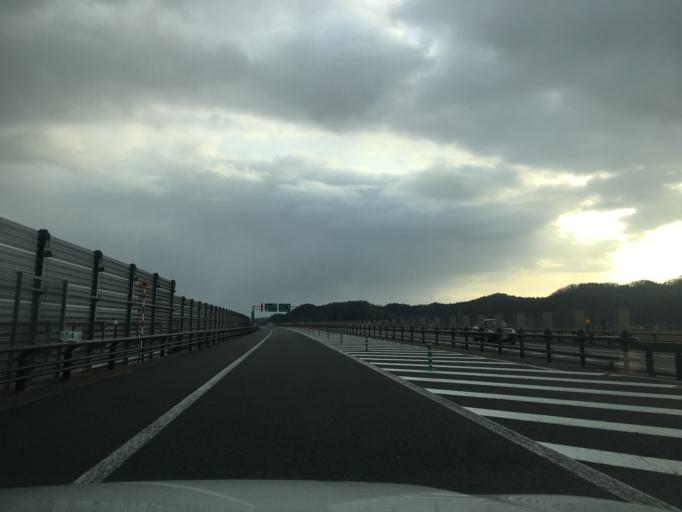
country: JP
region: Yamagata
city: Tsuruoka
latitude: 38.7116
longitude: 139.7489
